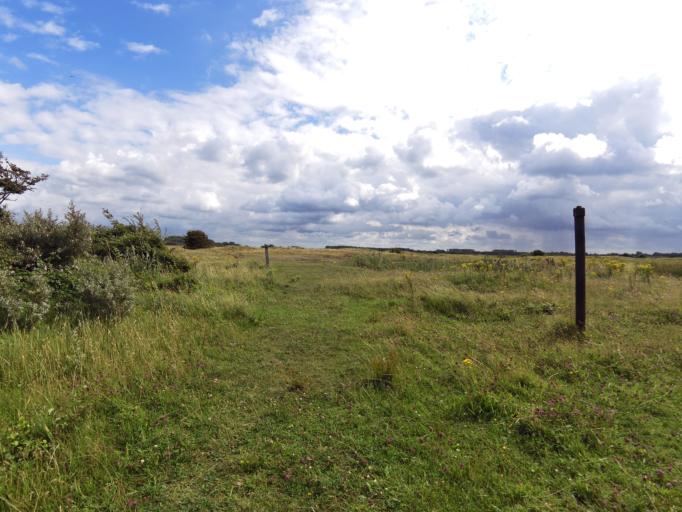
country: NL
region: South Holland
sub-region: Gemeente Goeree-Overflakkee
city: Ouddorp
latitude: 51.8308
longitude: 3.9443
